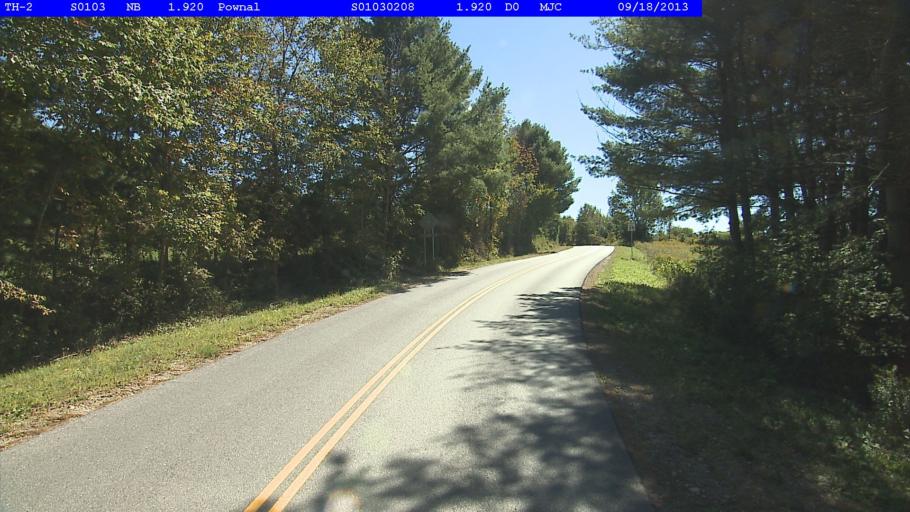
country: US
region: Vermont
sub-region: Bennington County
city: Bennington
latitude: 42.8024
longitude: -73.2376
